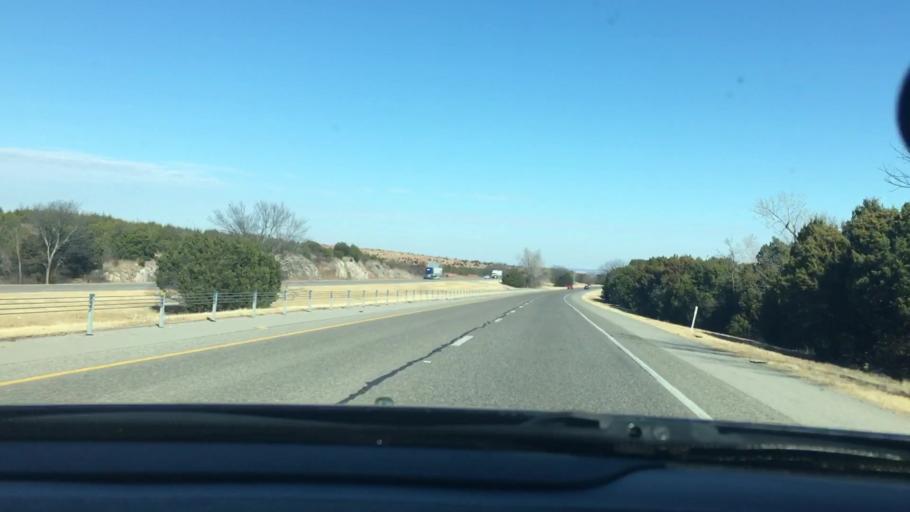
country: US
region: Oklahoma
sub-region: Murray County
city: Davis
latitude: 34.4133
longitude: -97.1380
